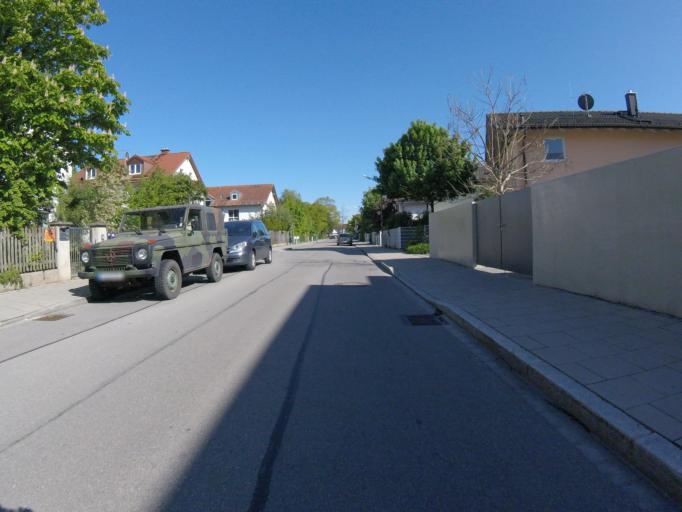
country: DE
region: Bavaria
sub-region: Upper Bavaria
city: Ottobrunn
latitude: 48.0645
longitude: 11.6754
